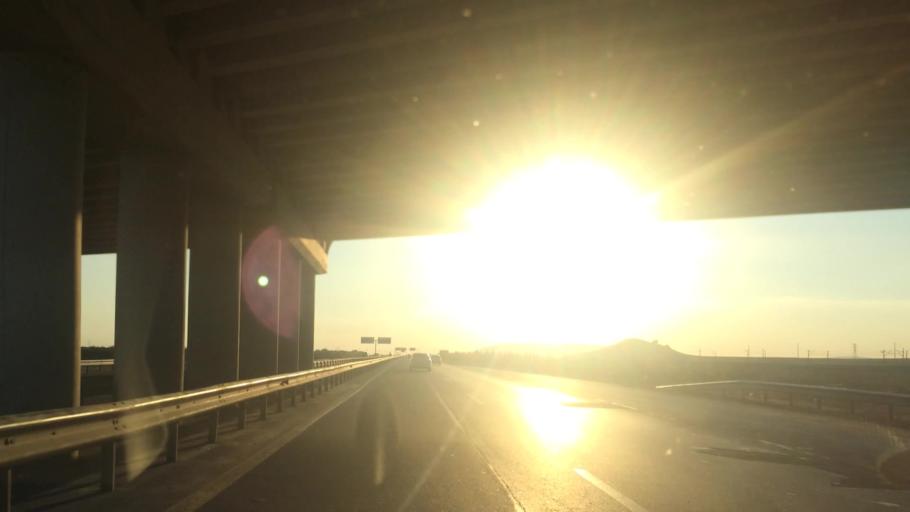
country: AZ
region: Baki
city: Qobustan
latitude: 39.9541
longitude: 49.3784
